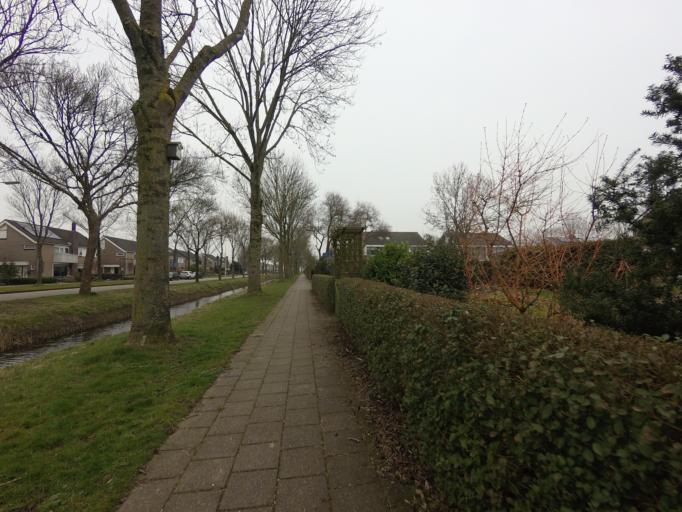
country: NL
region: Friesland
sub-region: Gemeente Franekeradeel
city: Franeker
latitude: 53.1893
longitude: 5.5615
